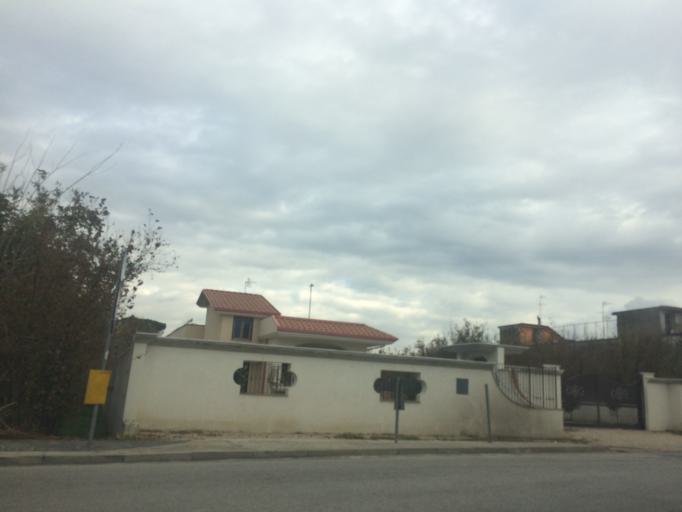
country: IT
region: Campania
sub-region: Provincia di Napoli
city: Piazzolla
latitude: 40.9050
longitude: 14.5288
